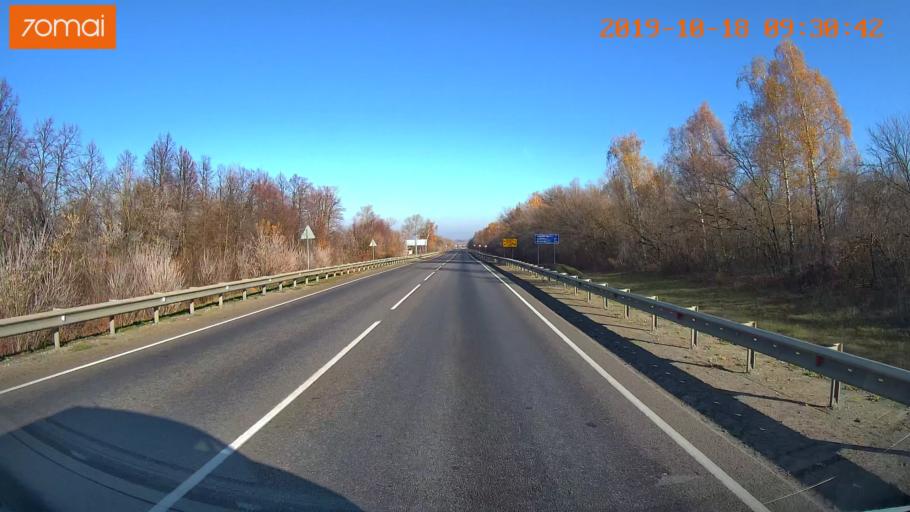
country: RU
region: Tula
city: Yefremov
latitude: 53.1413
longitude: 38.1594
